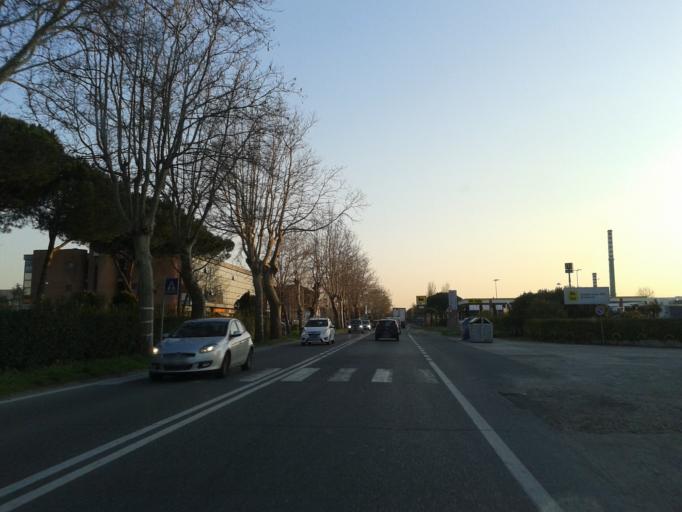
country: IT
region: Tuscany
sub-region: Provincia di Livorno
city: Livorno
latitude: 43.5905
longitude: 10.3478
